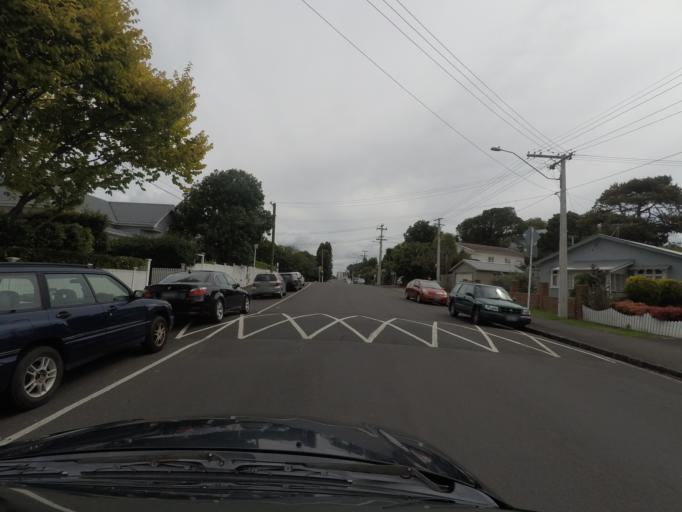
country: NZ
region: Auckland
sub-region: Auckland
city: Auckland
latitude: -36.8738
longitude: 174.7506
